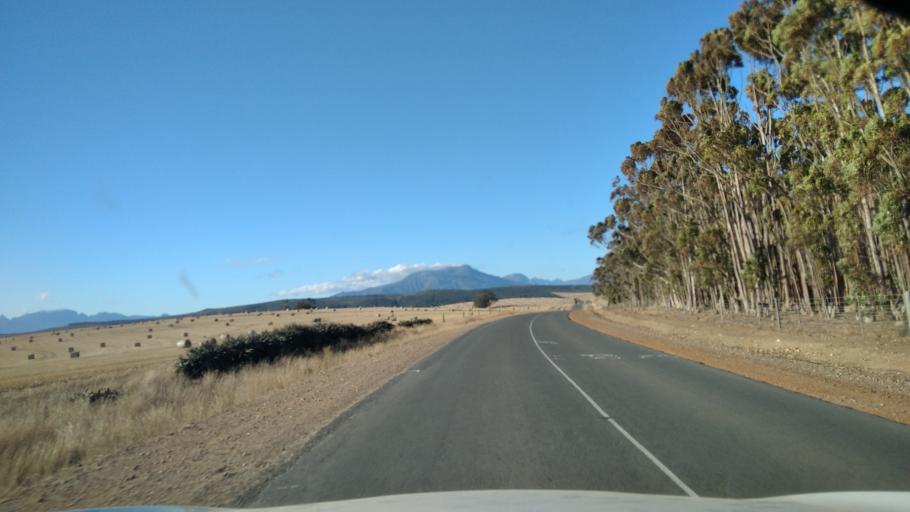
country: ZA
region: Western Cape
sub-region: Overberg District Municipality
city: Caledon
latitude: -34.1406
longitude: 19.2963
